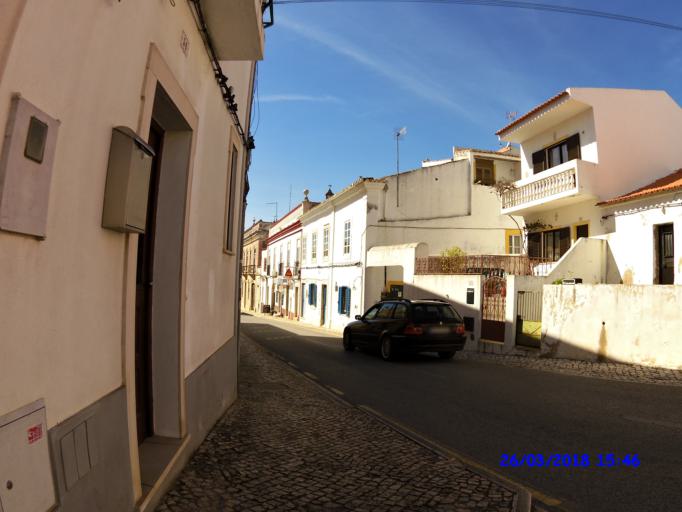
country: PT
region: Faro
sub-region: Loule
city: Boliqueime
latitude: 37.1760
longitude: -8.1998
